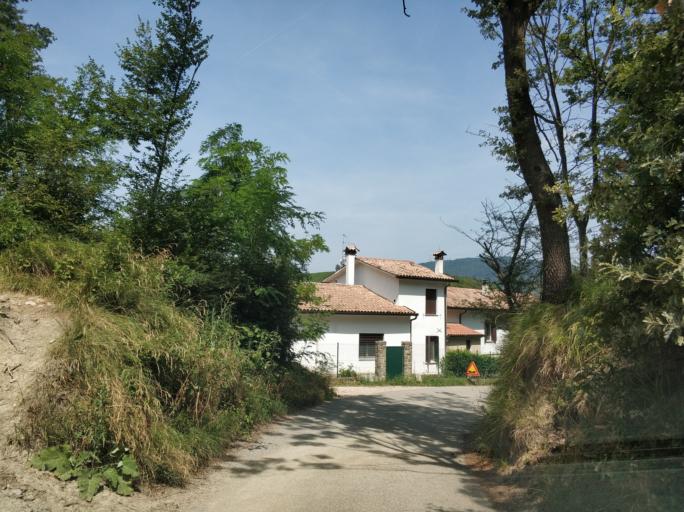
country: IT
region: Veneto
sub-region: Provincia di Padova
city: Arqua Petrarca
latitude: 45.2850
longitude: 11.7037
